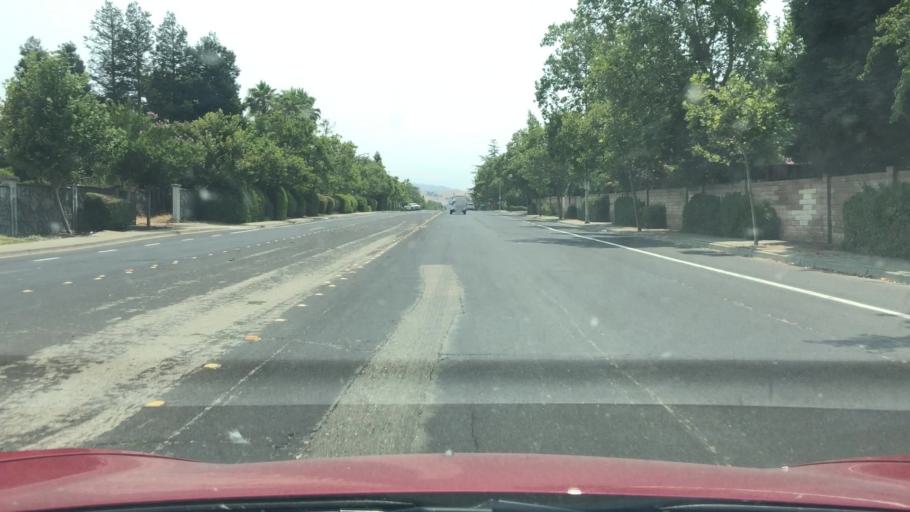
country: US
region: California
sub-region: Alameda County
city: Livermore
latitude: 37.6646
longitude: -121.7682
